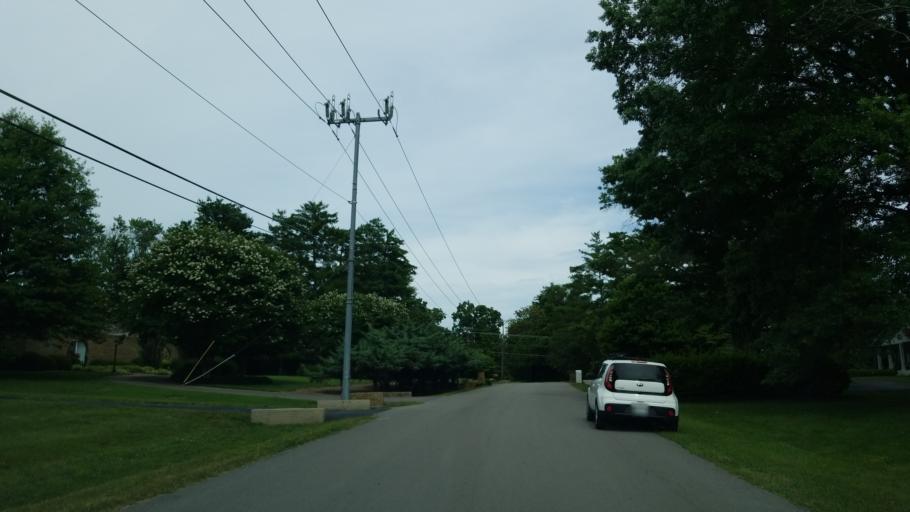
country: US
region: Tennessee
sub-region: Davidson County
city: Forest Hills
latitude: 36.0350
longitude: -86.8237
